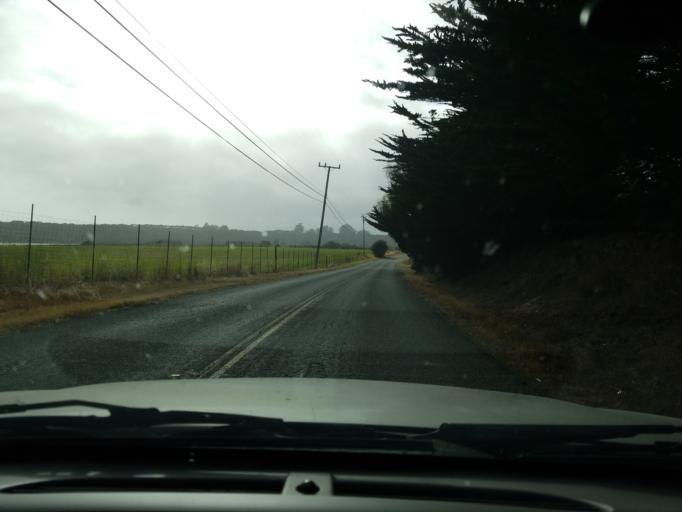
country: US
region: California
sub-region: Monterey County
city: Elkhorn
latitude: 36.8442
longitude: -121.7457
